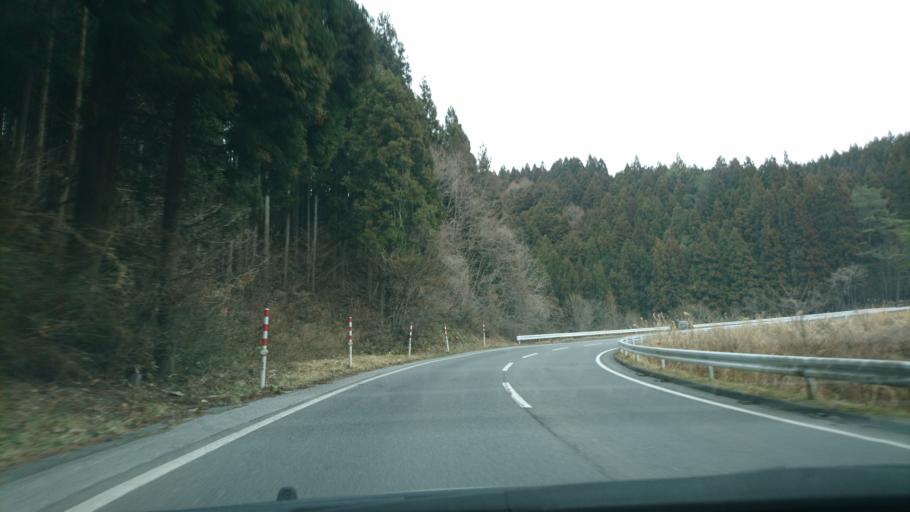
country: JP
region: Iwate
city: Tono
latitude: 39.2335
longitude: 141.5966
